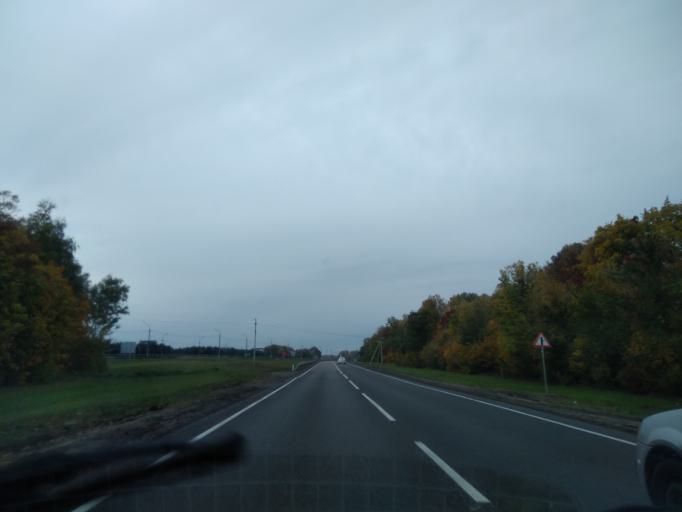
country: RU
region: Lipetsk
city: Zadonsk
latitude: 52.4374
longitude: 38.8156
